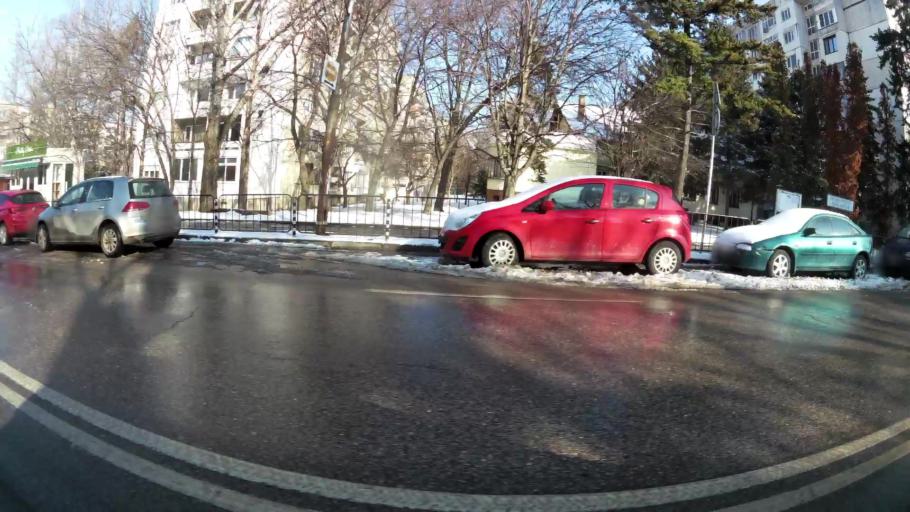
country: BG
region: Sofia-Capital
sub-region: Stolichna Obshtina
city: Sofia
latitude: 42.6610
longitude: 23.3468
